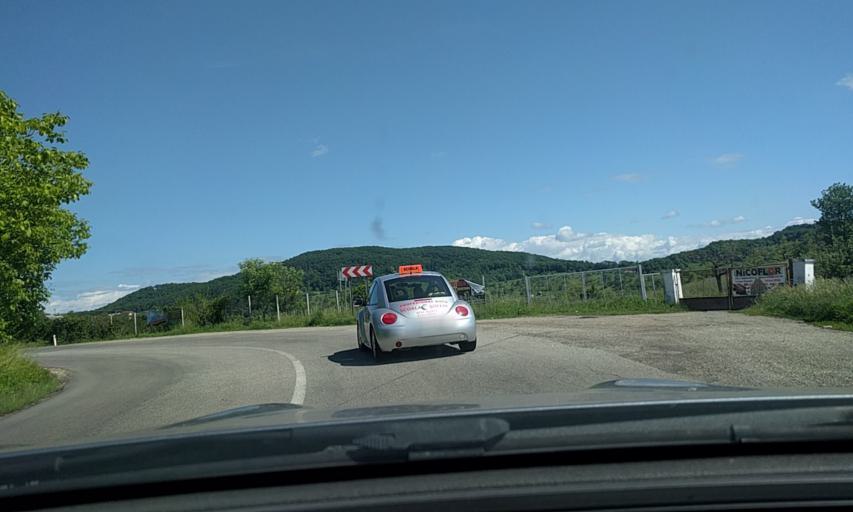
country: RO
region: Bistrita-Nasaud
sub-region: Municipiul Bistrita
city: Unirea
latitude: 47.1748
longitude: 24.4938
